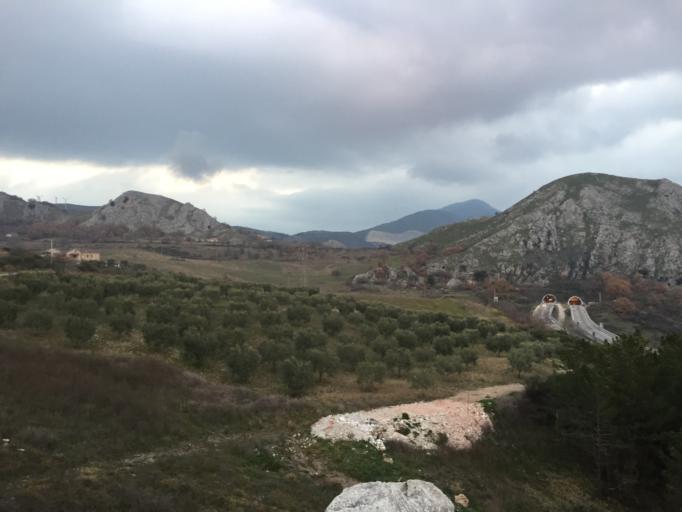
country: IT
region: Basilicate
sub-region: Provincia di Potenza
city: Vietri di Potenza
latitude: 40.6202
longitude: 15.4970
